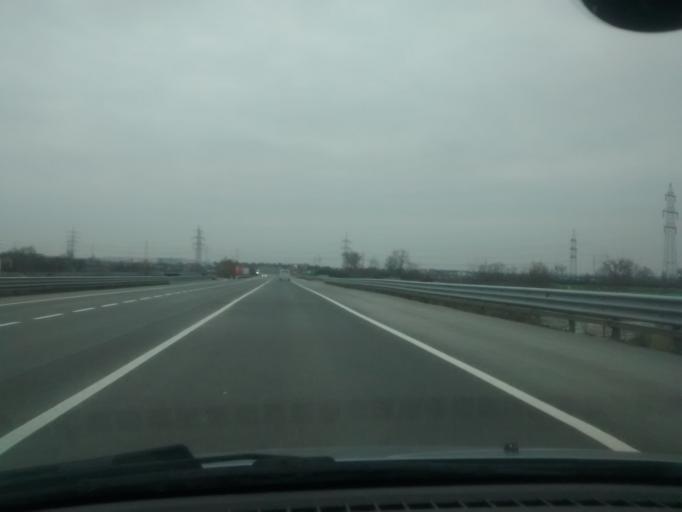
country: AT
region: Lower Austria
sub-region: Politischer Bezirk Wien-Umgebung
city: Leopoldsdorf
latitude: 48.0971
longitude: 16.3982
